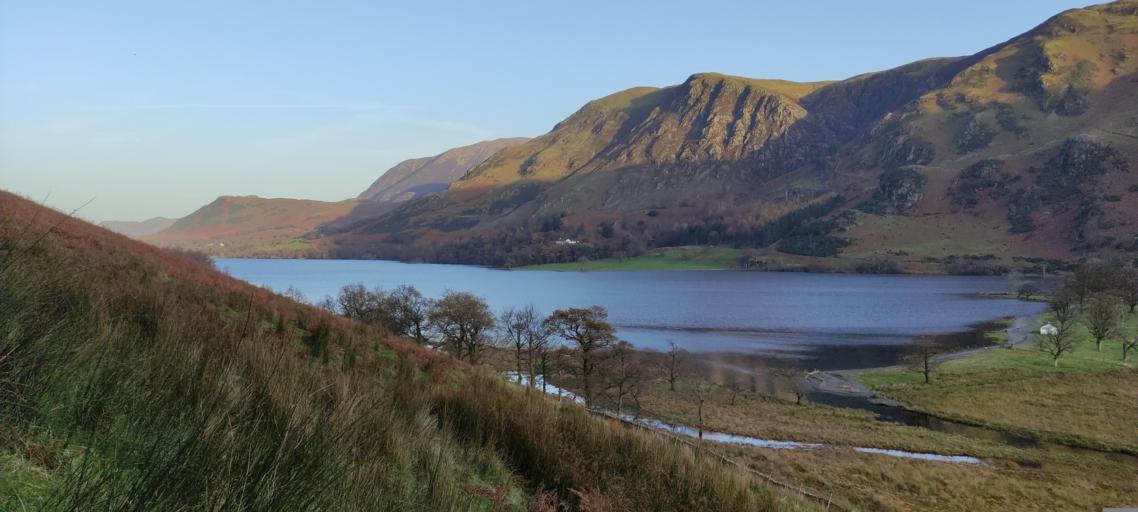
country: GB
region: England
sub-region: Cumbria
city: Keswick
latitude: 54.5216
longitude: -3.2555
